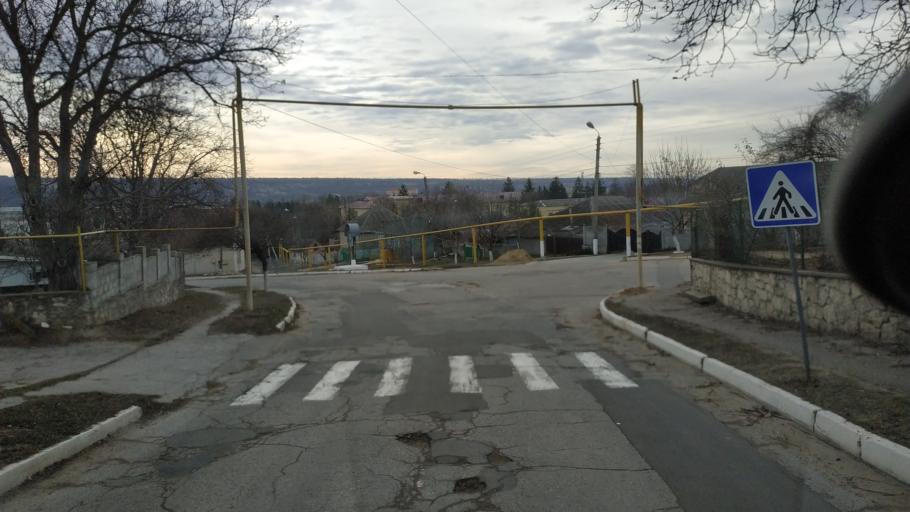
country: MD
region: Criuleni
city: Criuleni
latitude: 47.2163
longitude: 29.1590
